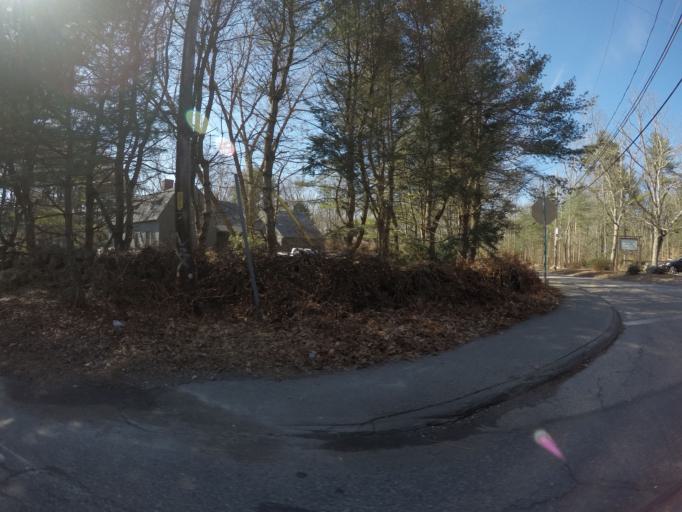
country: US
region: Massachusetts
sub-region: Bristol County
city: Easton
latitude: 42.0640
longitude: -71.1338
